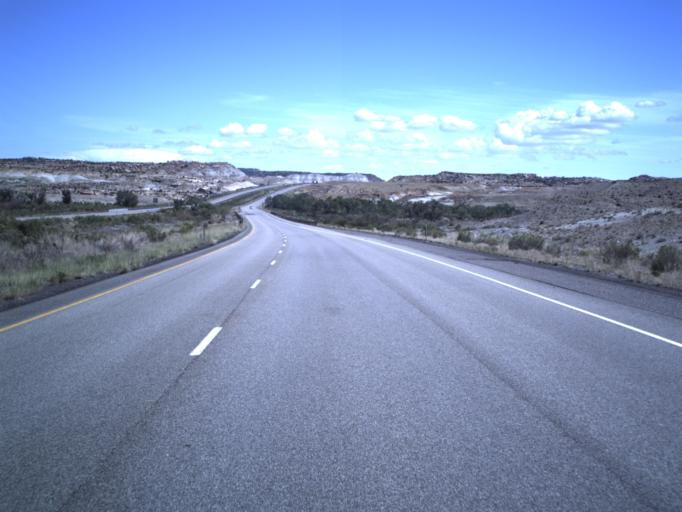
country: US
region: Utah
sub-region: Emery County
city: Ferron
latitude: 38.8119
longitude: -111.2043
